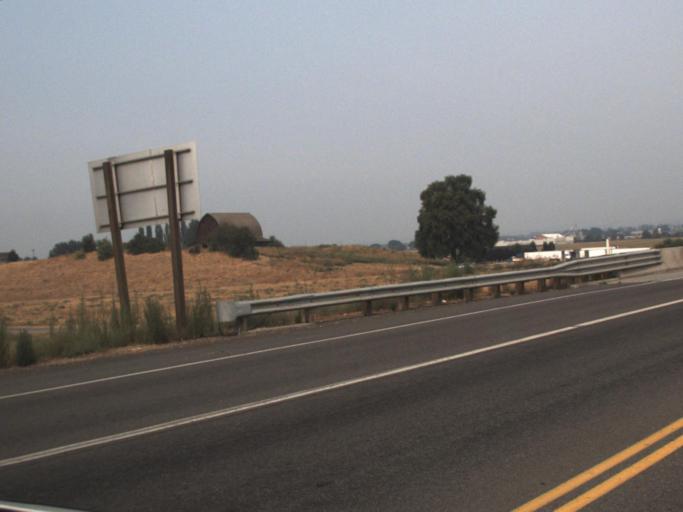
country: US
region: Washington
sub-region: Yakima County
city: Sunnyside
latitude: 46.3057
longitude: -119.9784
